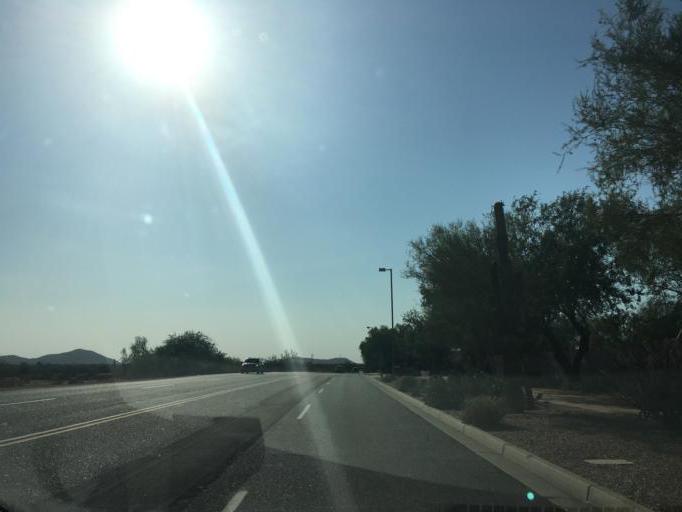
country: US
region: Arizona
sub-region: Maricopa County
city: Carefree
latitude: 33.6820
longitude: -111.9821
